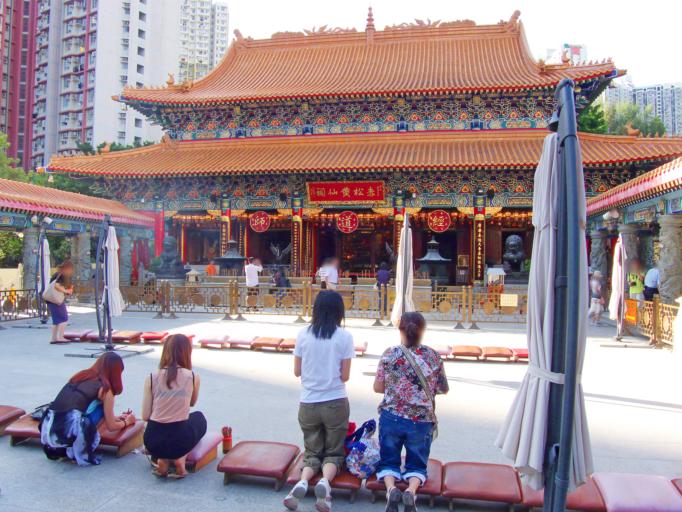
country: HK
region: Wong Tai Sin
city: Wong Tai Sin
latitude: 22.3425
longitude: 114.1935
